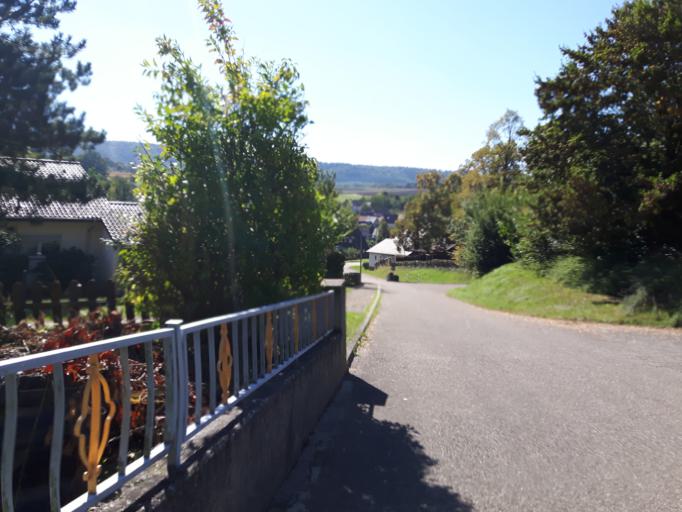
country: DE
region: Baden-Wuerttemberg
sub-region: Regierungsbezirk Stuttgart
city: Zaberfeld
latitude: 49.0606
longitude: 8.9502
